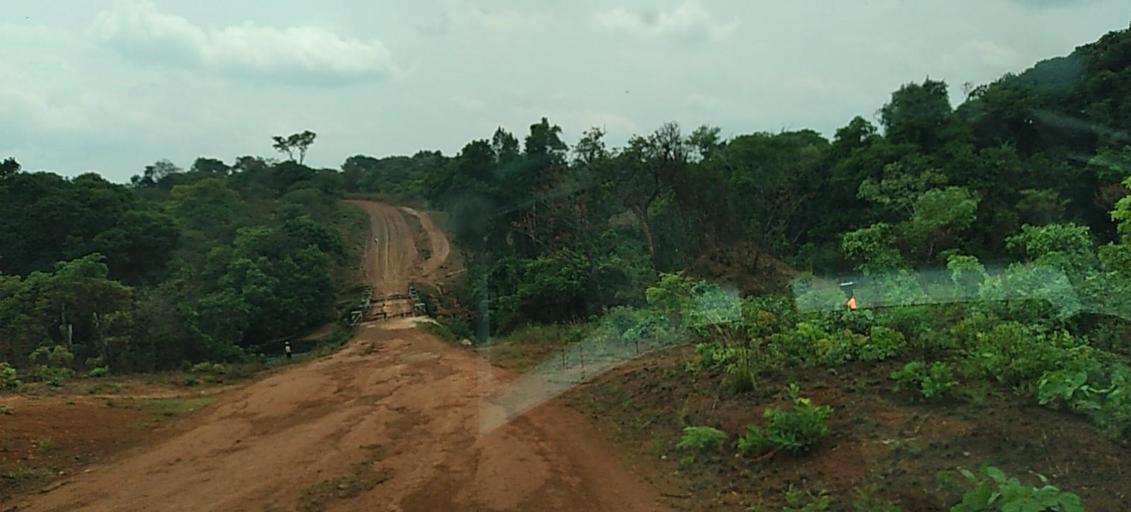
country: ZM
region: North-Western
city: Mwinilunga
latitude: -11.5120
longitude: 24.7903
